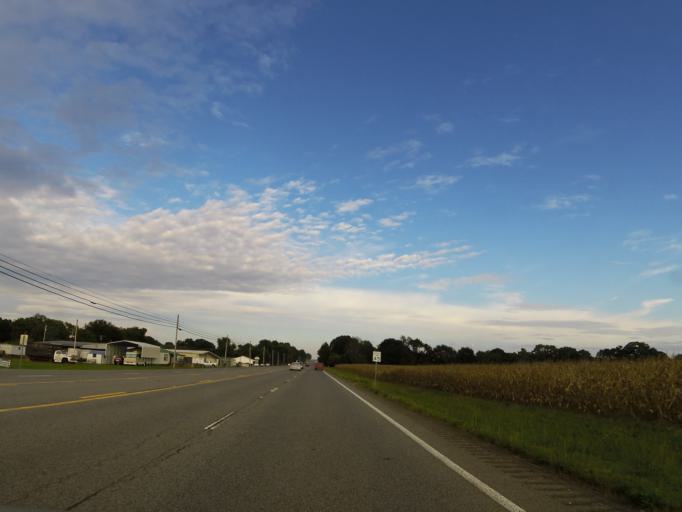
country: US
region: Alabama
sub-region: Lauderdale County
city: Rogersville
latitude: 34.8205
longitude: -87.2802
